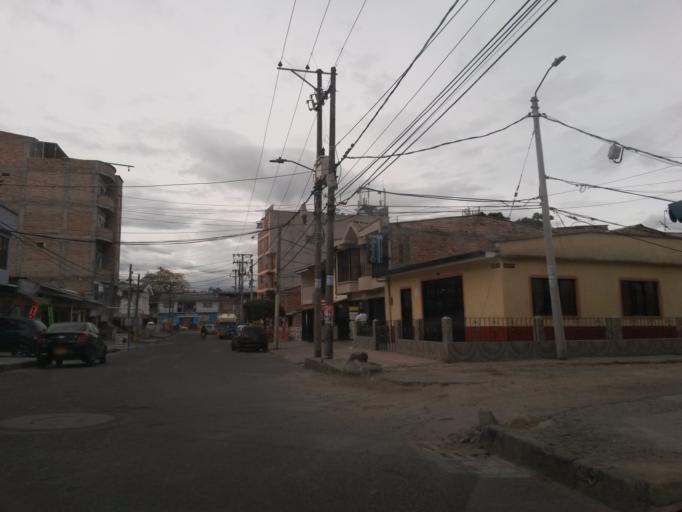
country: CO
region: Cauca
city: Popayan
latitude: 2.4450
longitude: -76.6182
